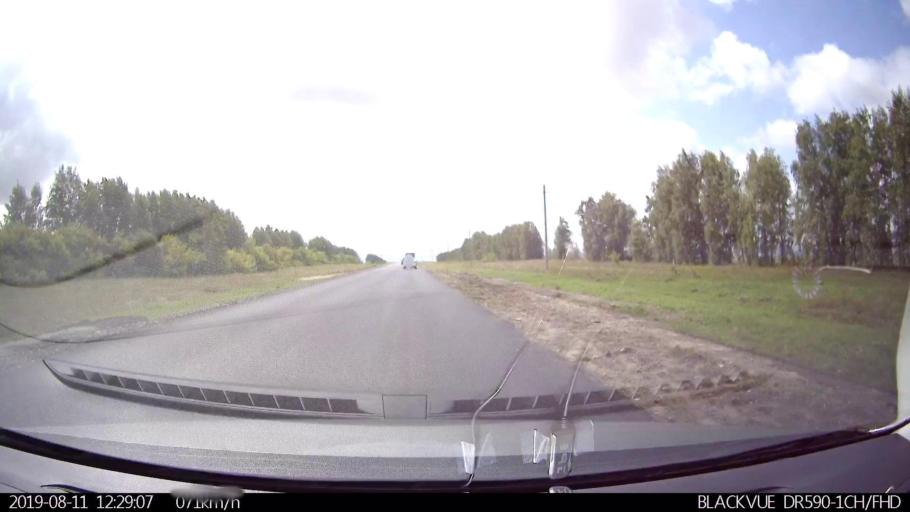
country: RU
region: Ulyanovsk
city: Ignatovka
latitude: 53.8377
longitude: 47.9054
